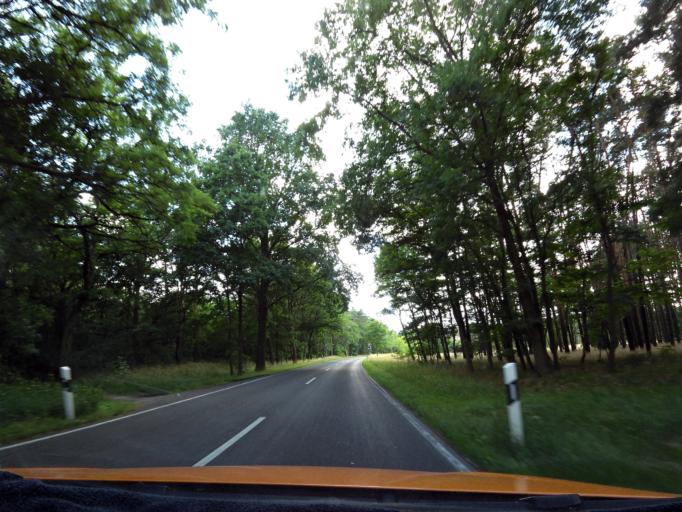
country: DE
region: Brandenburg
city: Erkner
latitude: 52.3121
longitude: 13.7459
